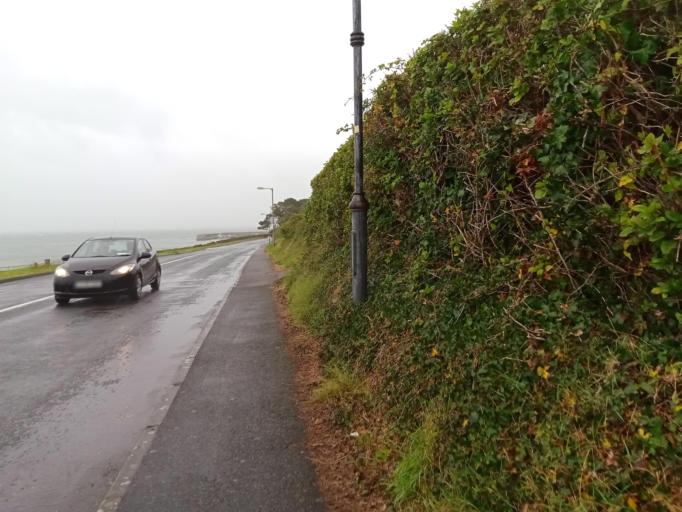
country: IE
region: Munster
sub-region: Waterford
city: Dungarvan
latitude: 52.0530
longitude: -7.5521
